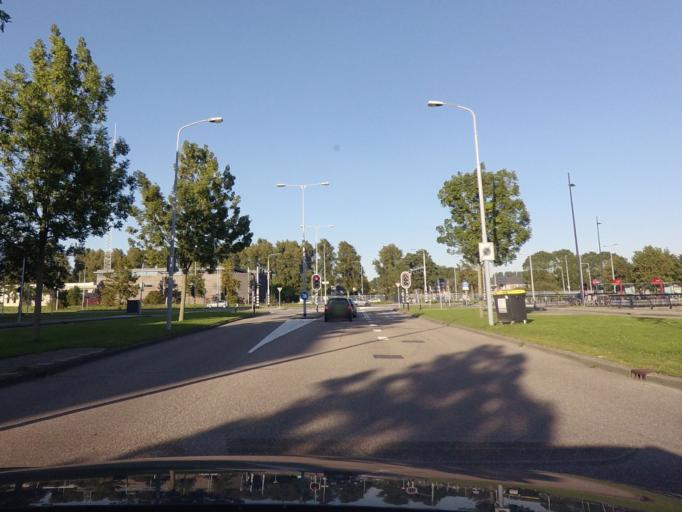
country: NL
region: North Holland
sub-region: Gemeente Haarlemmermeer
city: Hoofddorp
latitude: 52.2952
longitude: 4.6823
